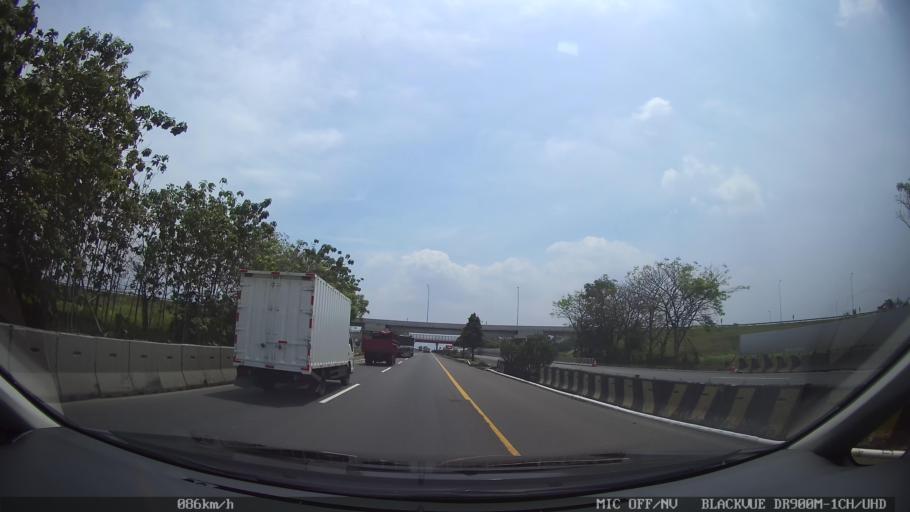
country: ID
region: Banten
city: Serang
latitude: -6.1386
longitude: 106.2462
